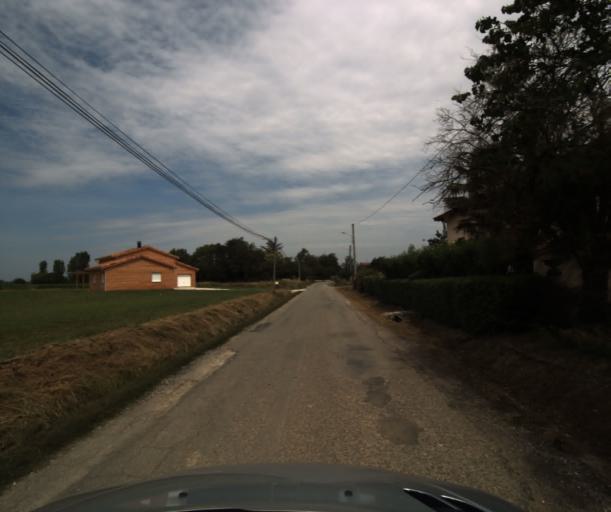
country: FR
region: Midi-Pyrenees
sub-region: Departement de la Haute-Garonne
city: Lacasse
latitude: 43.4159
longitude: 1.2714
